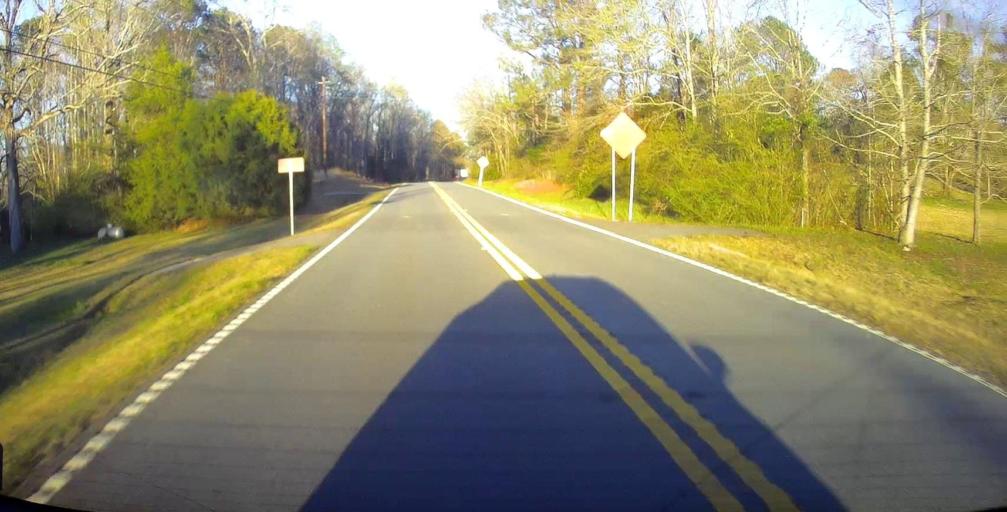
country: US
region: Georgia
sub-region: Harris County
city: Hamilton
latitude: 32.6557
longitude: -84.8562
